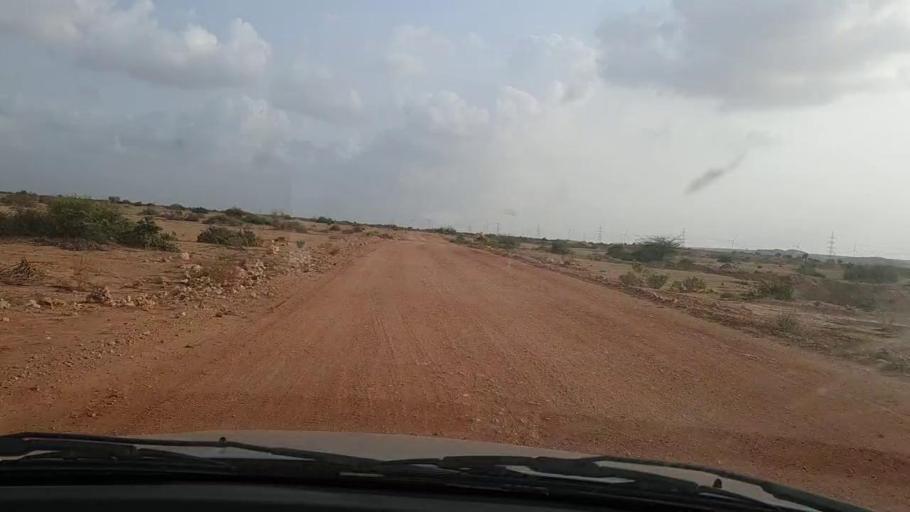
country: PK
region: Sindh
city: Thatta
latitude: 25.0782
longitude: 67.8942
